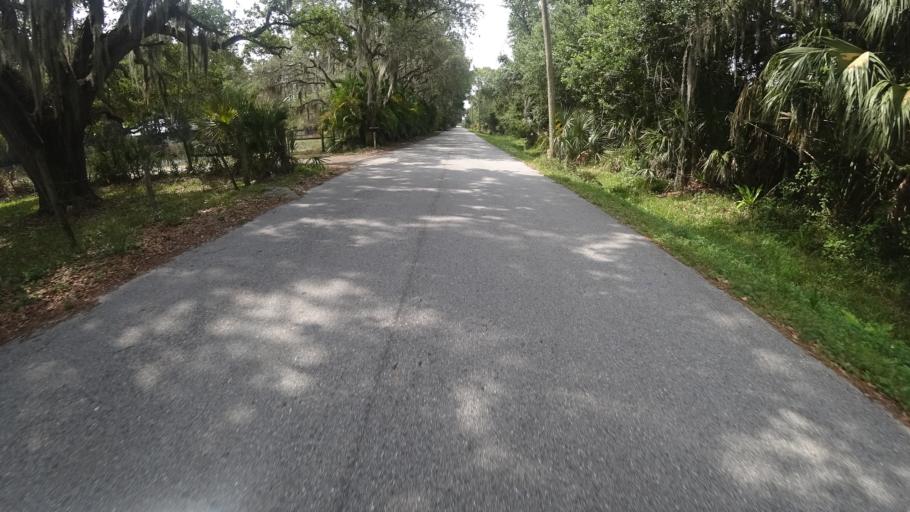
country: US
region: Florida
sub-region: Sarasota County
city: North Sarasota
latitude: 27.4009
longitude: -82.5301
